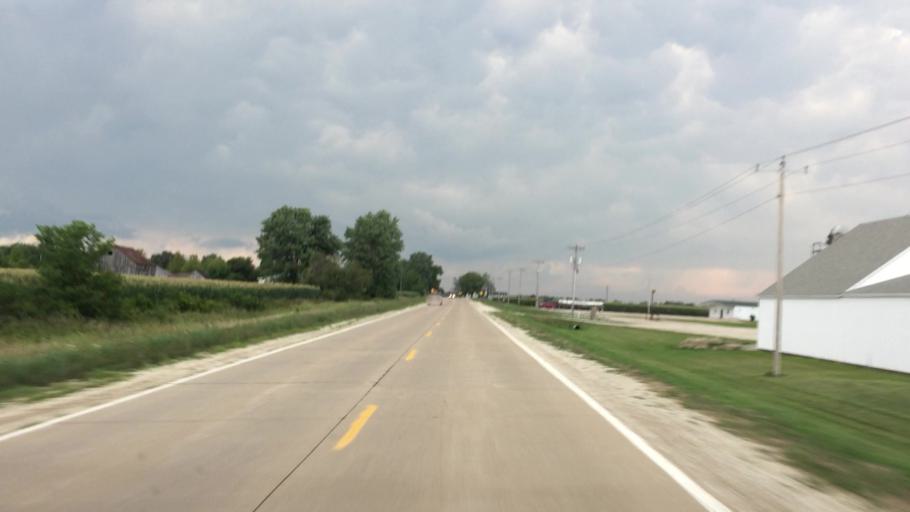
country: US
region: Iowa
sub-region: Lee County
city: Fort Madison
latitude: 40.7369
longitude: -91.3283
